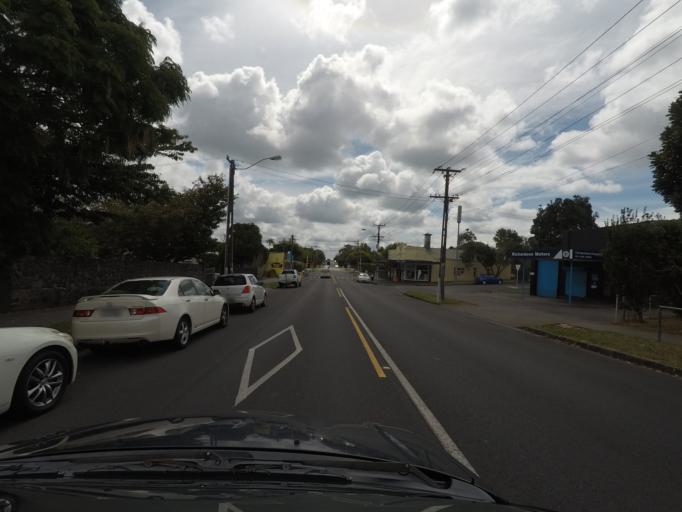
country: NZ
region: Auckland
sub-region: Auckland
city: Rosebank
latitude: -36.8927
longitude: 174.7138
